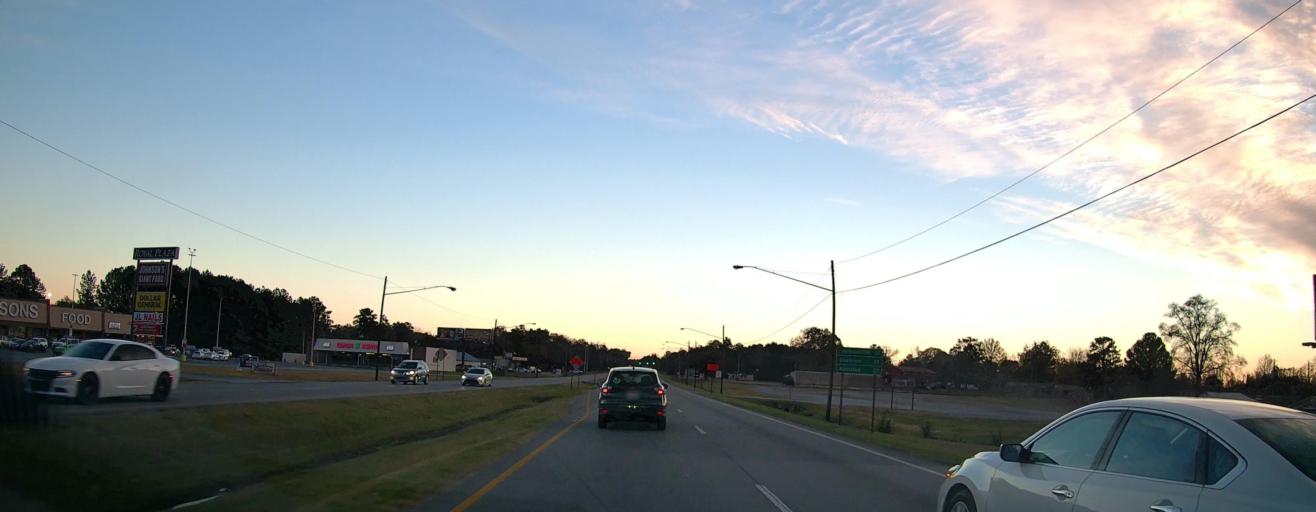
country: US
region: Alabama
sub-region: Etowah County
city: Gadsden
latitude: 33.9985
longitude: -85.9683
